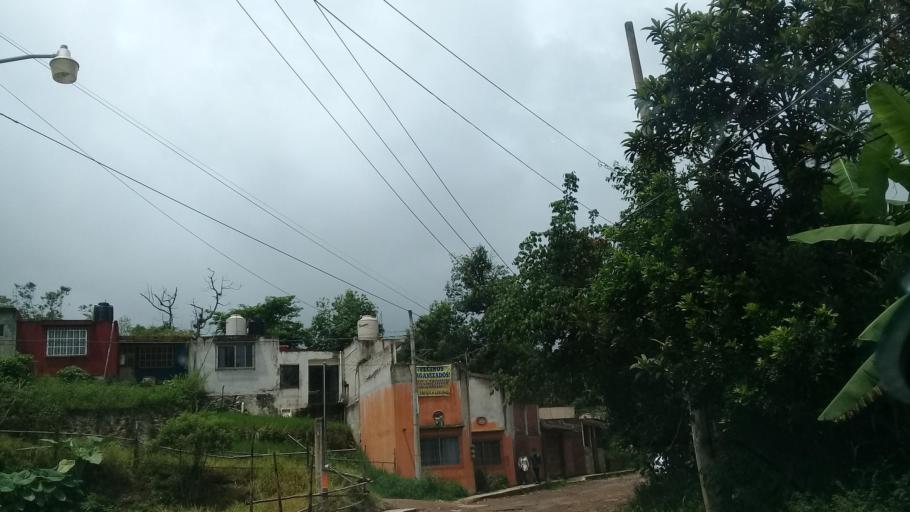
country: MX
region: Veracruz
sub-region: Xalapa
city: Colonia Santa Barbara
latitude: 19.4972
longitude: -96.8706
